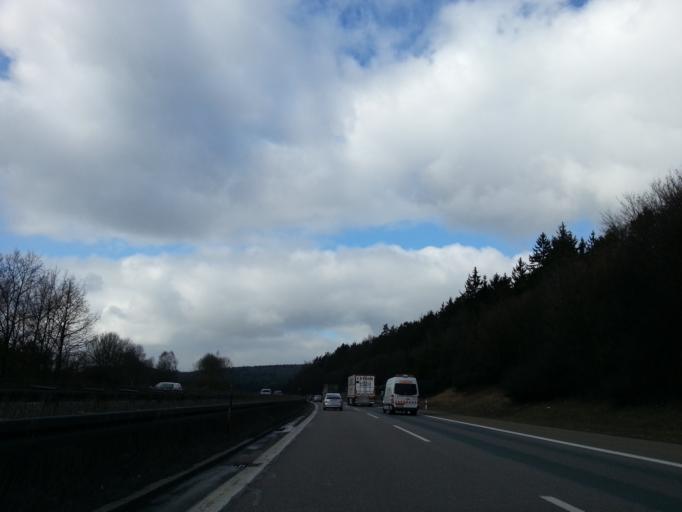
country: DE
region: Bavaria
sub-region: Upper Palatinate
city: Velburg
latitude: 49.1949
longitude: 11.6814
